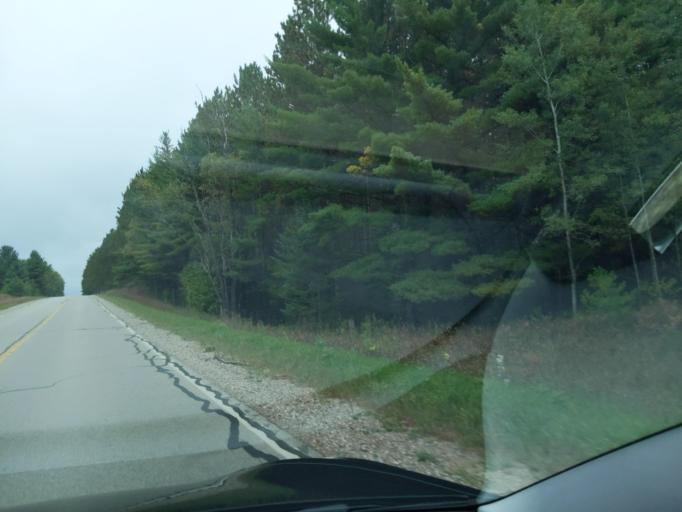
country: US
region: Michigan
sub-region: Grand Traverse County
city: Kingsley
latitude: 44.6200
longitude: -85.3532
